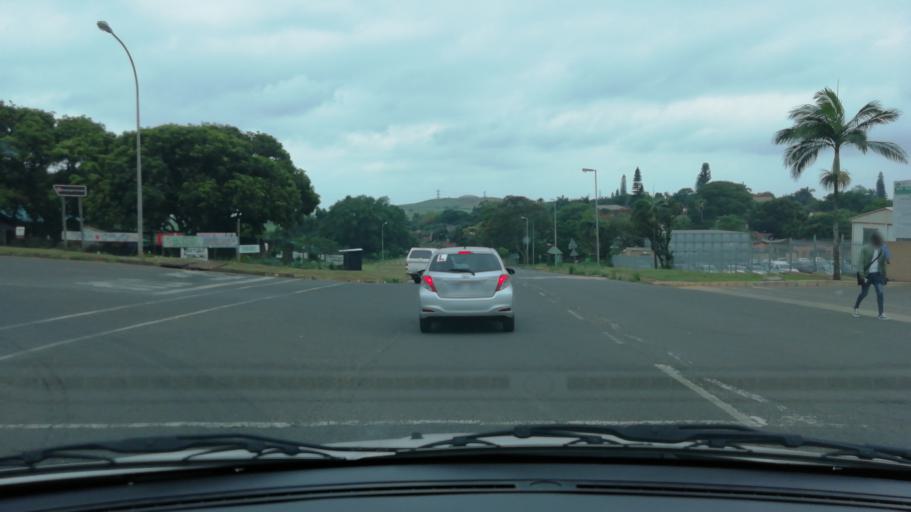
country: ZA
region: KwaZulu-Natal
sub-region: uThungulu District Municipality
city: Empangeni
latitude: -28.7393
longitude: 31.8957
